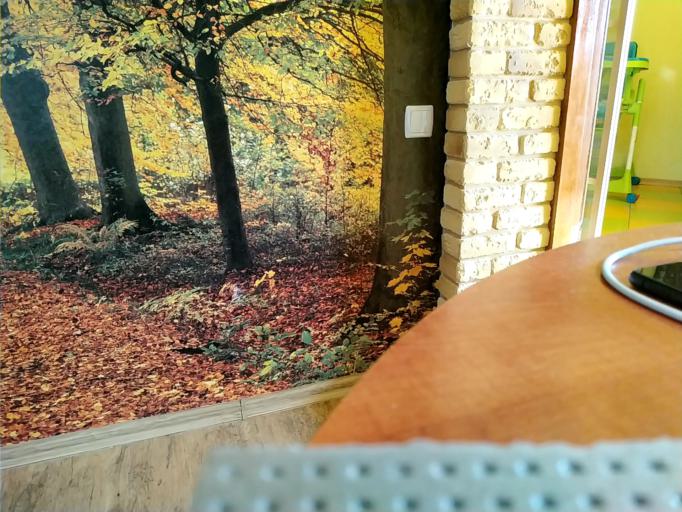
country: RU
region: Tverskaya
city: Kalashnikovo
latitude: 57.3472
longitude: 35.2127
